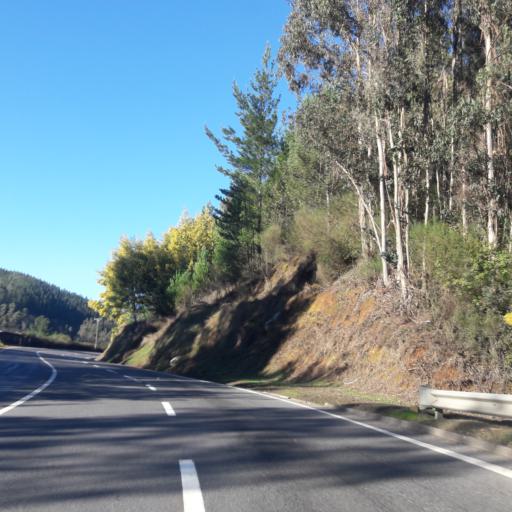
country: CL
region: Biobio
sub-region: Provincia de Biobio
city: La Laja
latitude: -37.2616
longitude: -72.9614
